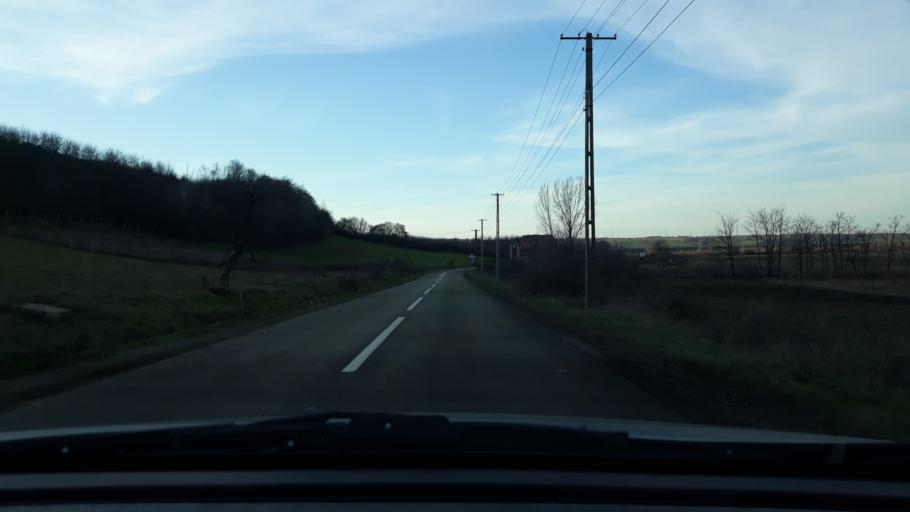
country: RO
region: Bihor
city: Foglas
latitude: 47.2310
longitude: 22.5437
